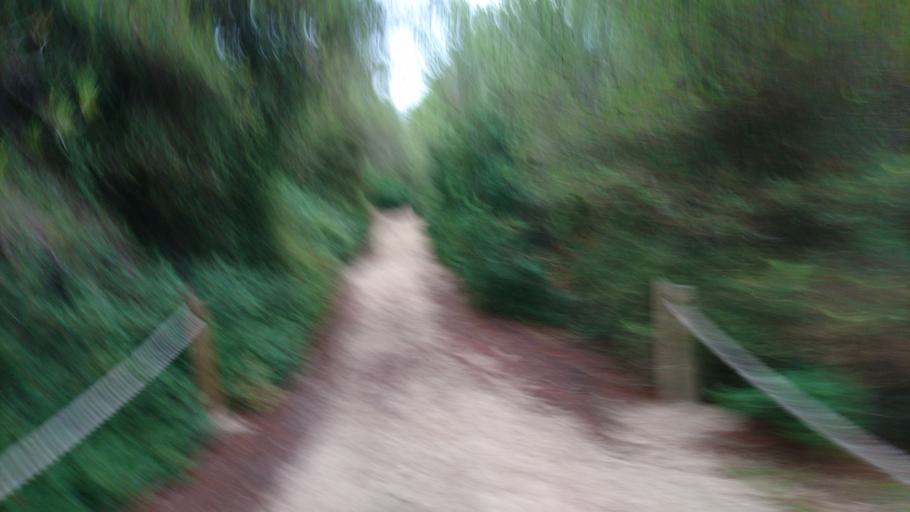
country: ES
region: Balearic Islands
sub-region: Illes Balears
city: Port d'Alcudia
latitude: 39.7756
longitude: 3.1393
